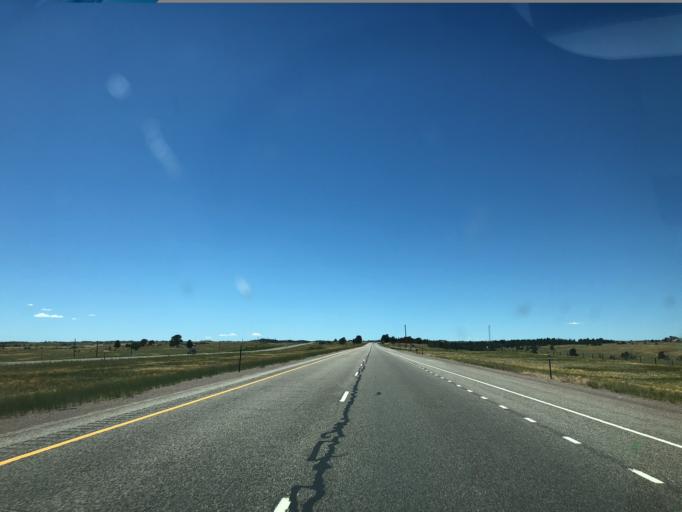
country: US
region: Wyoming
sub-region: Albany County
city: Laramie
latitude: 41.1258
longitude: -105.3129
